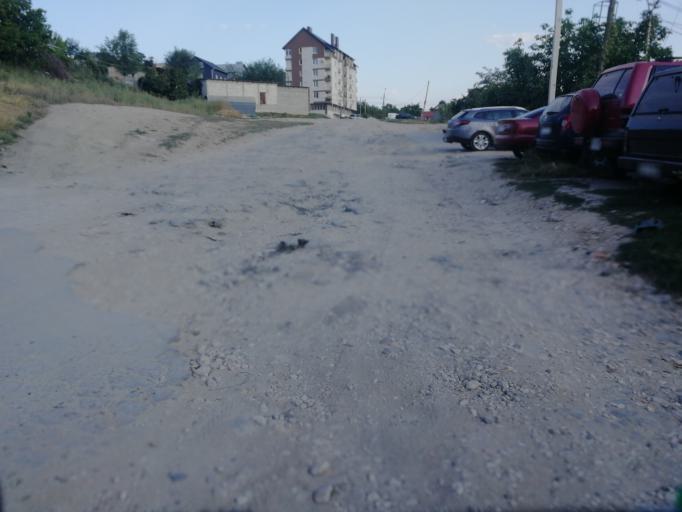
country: MD
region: Chisinau
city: Chisinau
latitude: 47.0280
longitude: 28.8704
